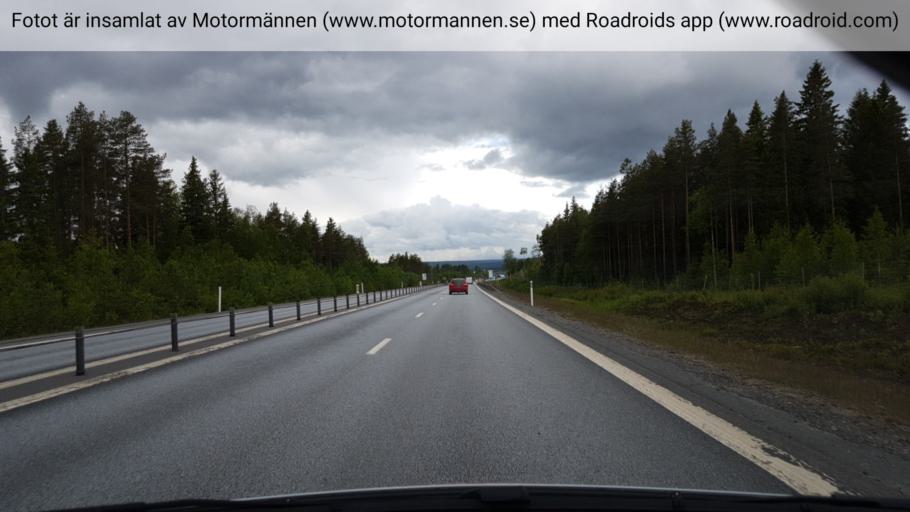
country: SE
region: Vaesterbotten
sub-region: Nordmalings Kommun
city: Nordmaling
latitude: 63.5814
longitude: 19.5217
